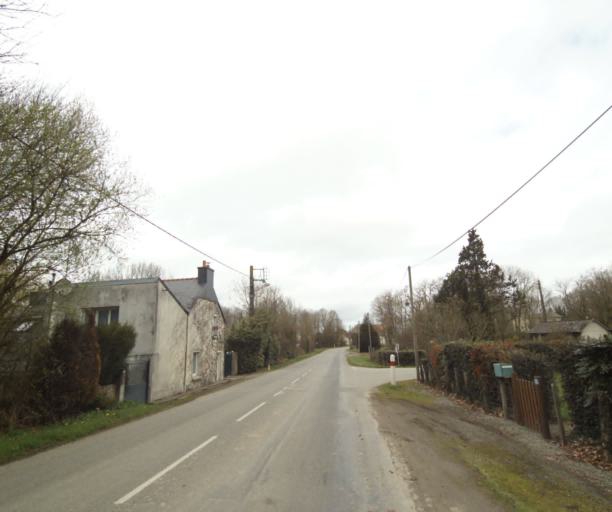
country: FR
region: Pays de la Loire
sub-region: Departement de la Loire-Atlantique
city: Bouvron
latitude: 47.4236
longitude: -1.8524
